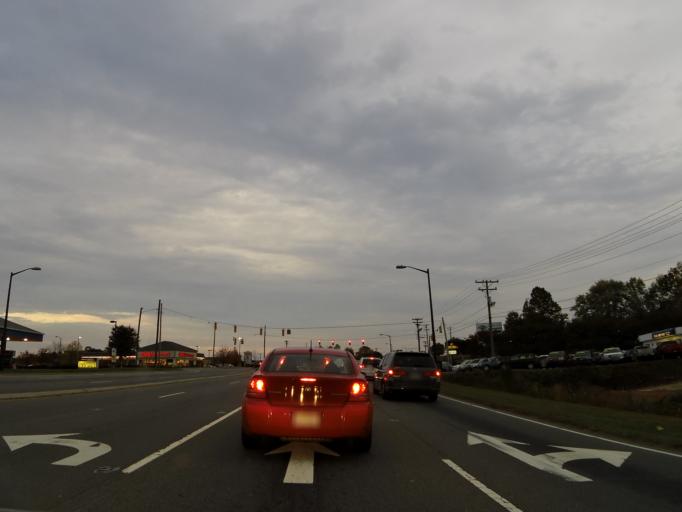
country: US
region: North Carolina
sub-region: Catawba County
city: Longview
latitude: 35.7482
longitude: -81.3672
